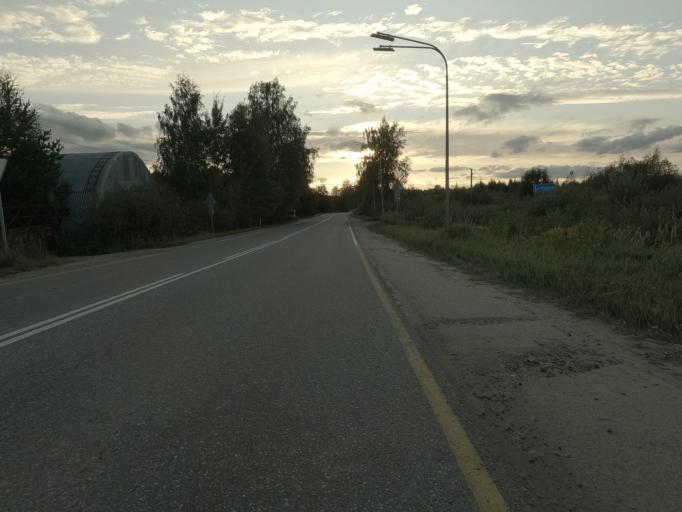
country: RU
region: Leningrad
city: Mga
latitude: 59.7539
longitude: 31.0308
